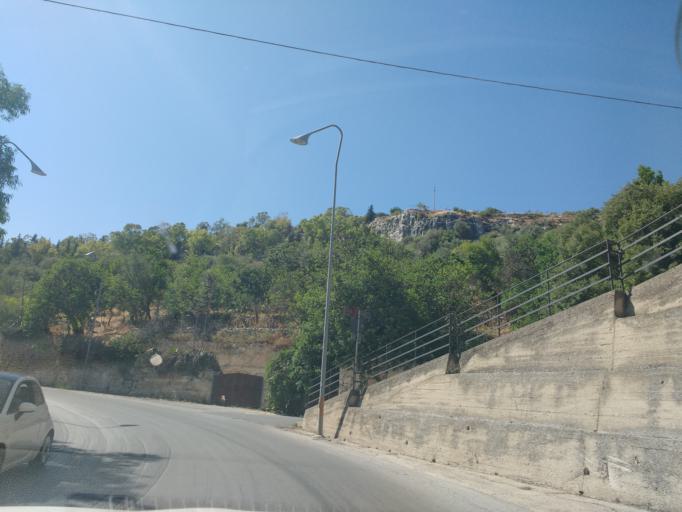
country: IT
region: Sicily
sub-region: Ragusa
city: Modica
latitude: 36.8683
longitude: 14.7564
